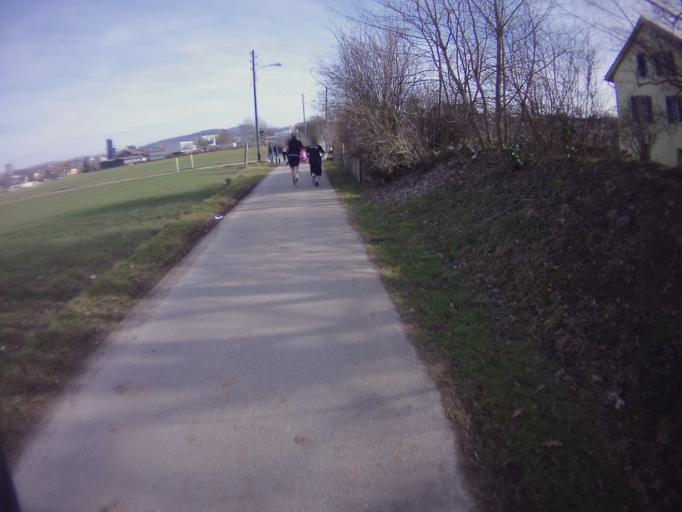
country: CH
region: Zurich
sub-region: Bezirk Dietikon
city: Dietikon / Almend
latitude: 47.4103
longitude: 8.3824
